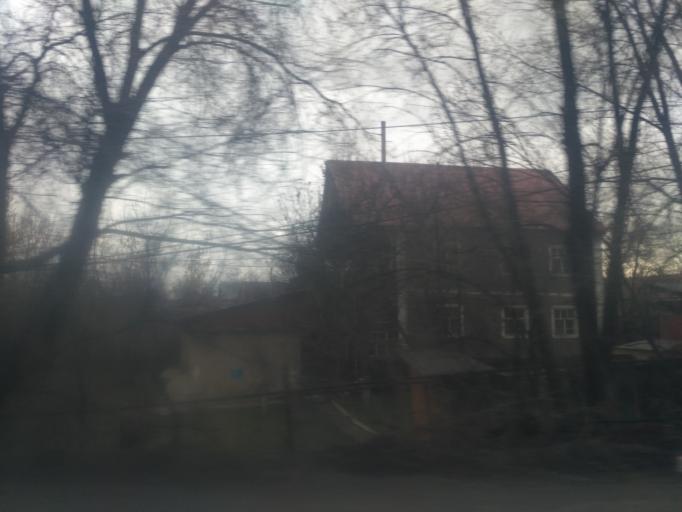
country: KZ
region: Almaty Oblysy
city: Burunday
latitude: 43.2187
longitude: 76.7436
